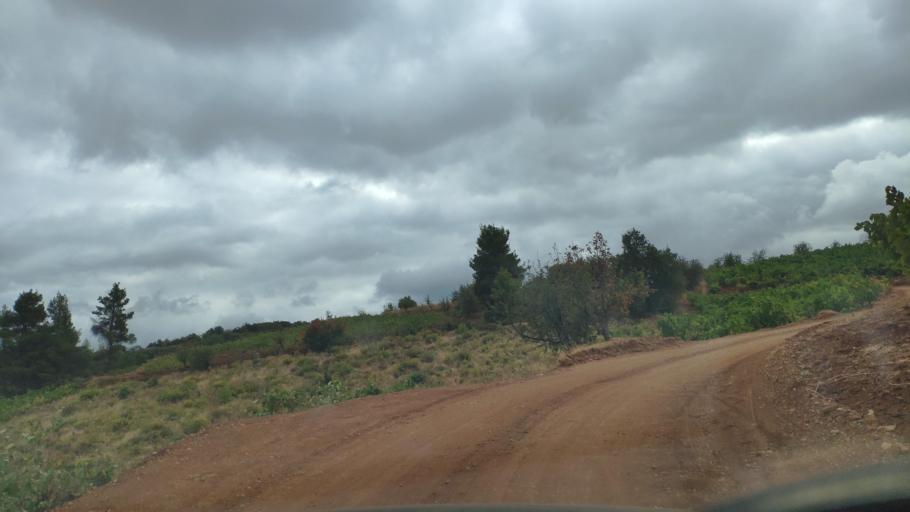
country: GR
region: West Greece
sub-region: Nomos Achaias
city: Temeni
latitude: 38.1655
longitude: 22.1479
